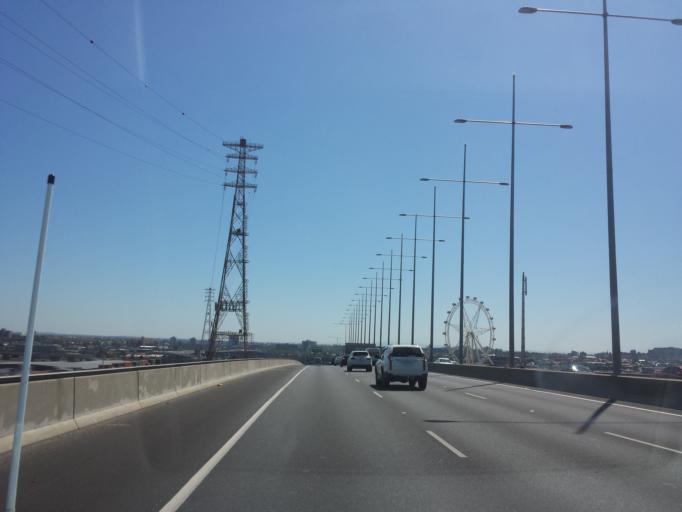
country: AU
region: Victoria
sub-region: Melbourne
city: Docklands
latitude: -37.8193
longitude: 144.9322
